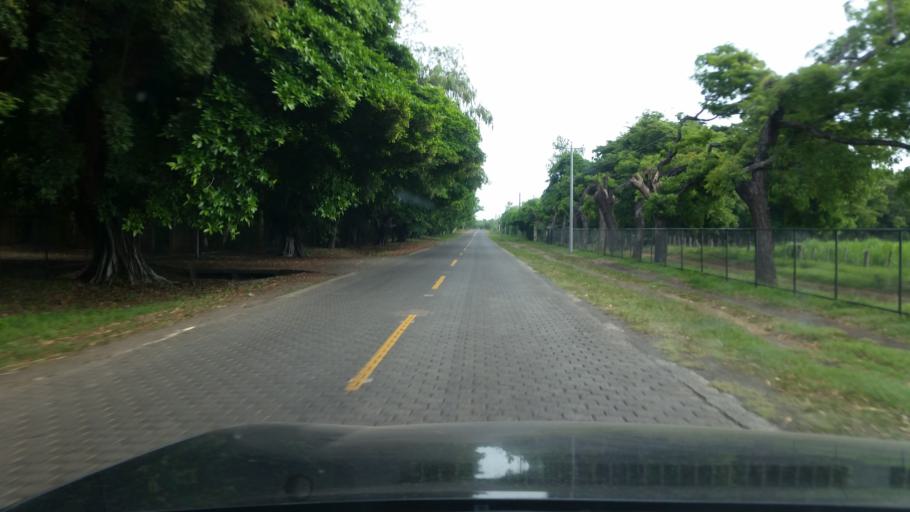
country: NI
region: Managua
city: Carlos Fonseca Amador
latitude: 12.0666
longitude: -86.5019
